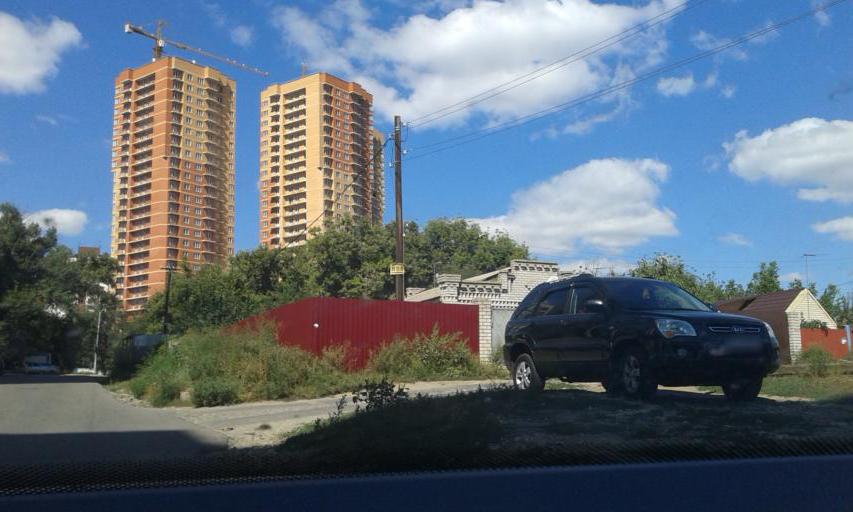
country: RU
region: Volgograd
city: Volgograd
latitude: 48.6781
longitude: 44.4781
